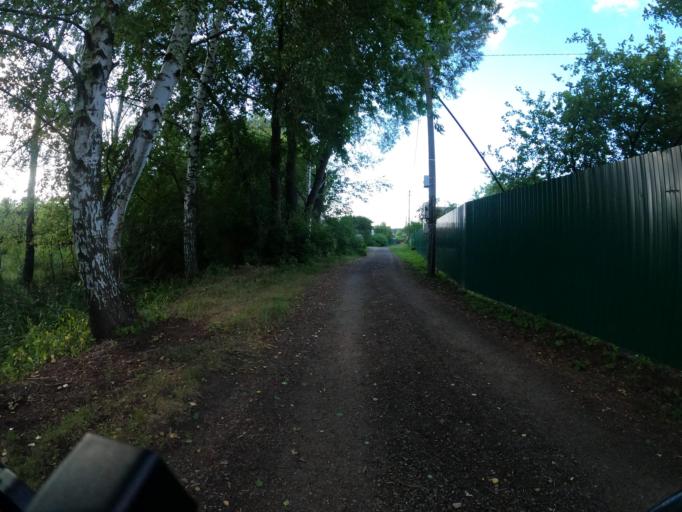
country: RU
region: Moskovskaya
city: Beloozerskiy
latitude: 55.4471
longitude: 38.5000
